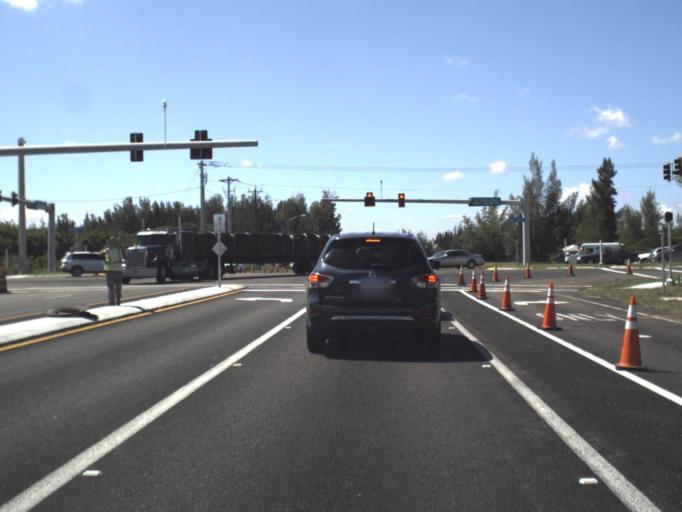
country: US
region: Florida
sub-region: Lee County
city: Pine Island Center
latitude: 26.6376
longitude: -82.0393
